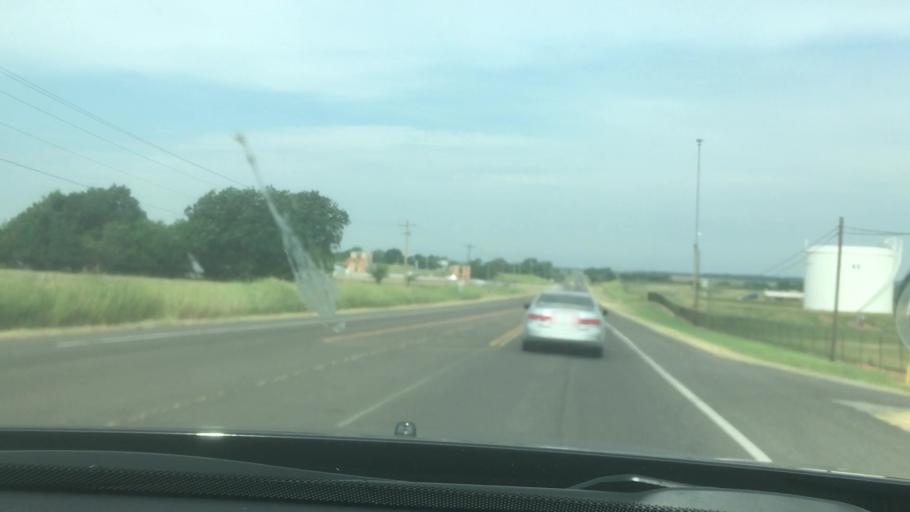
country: US
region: Oklahoma
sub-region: Garvin County
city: Maysville
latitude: 34.8192
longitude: -97.4449
